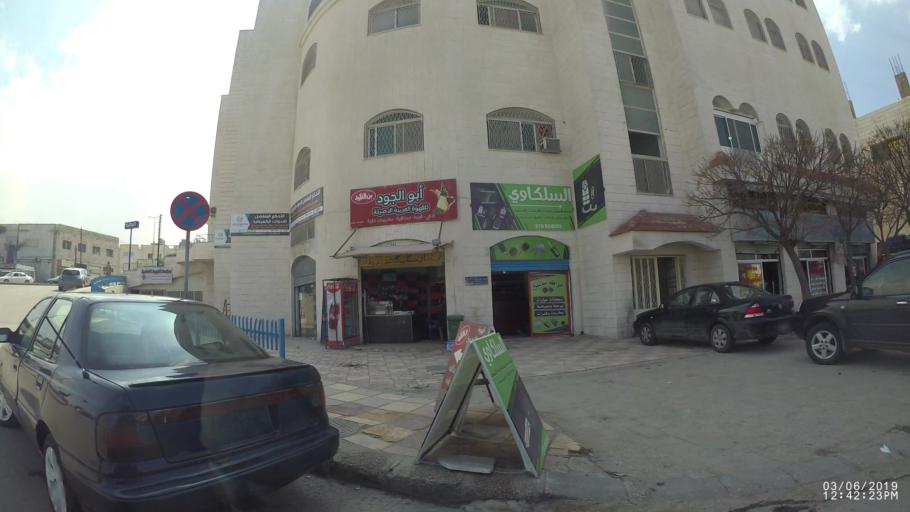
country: JO
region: Zarqa
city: Russeifa
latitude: 31.9901
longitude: 36.0014
